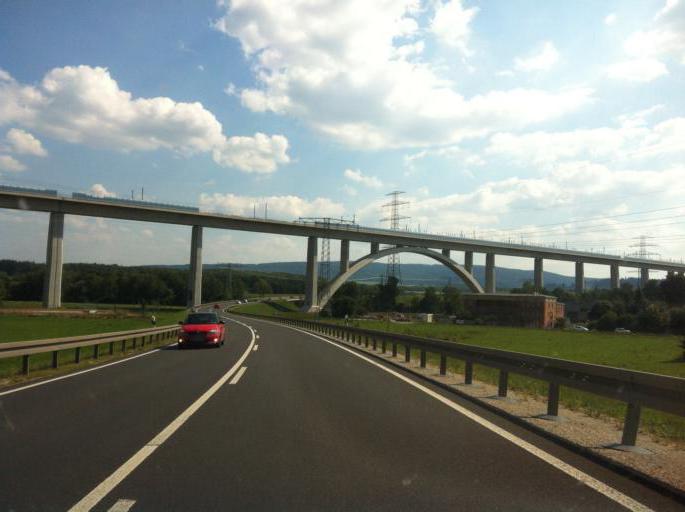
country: DE
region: Thuringia
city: Langewiesen
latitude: 50.6733
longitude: 10.9862
